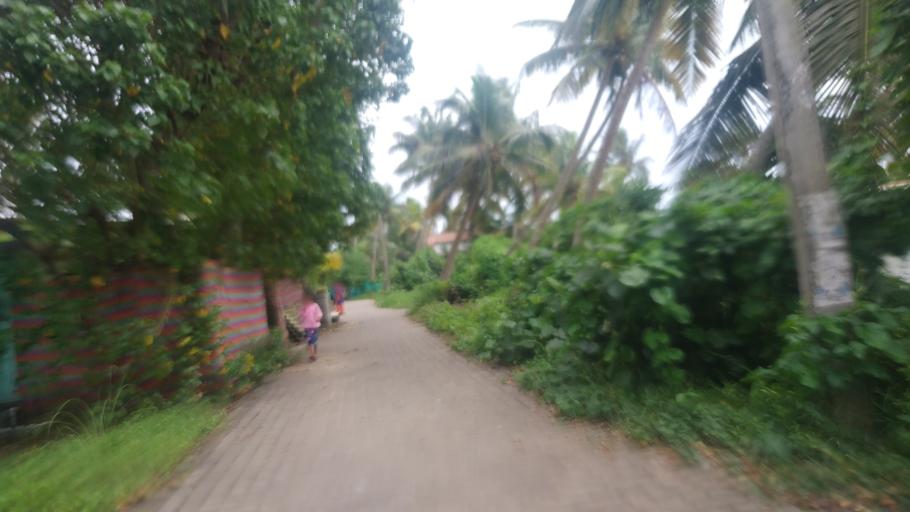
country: IN
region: Kerala
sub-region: Ernakulam
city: Cochin
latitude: 9.8706
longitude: 76.2753
